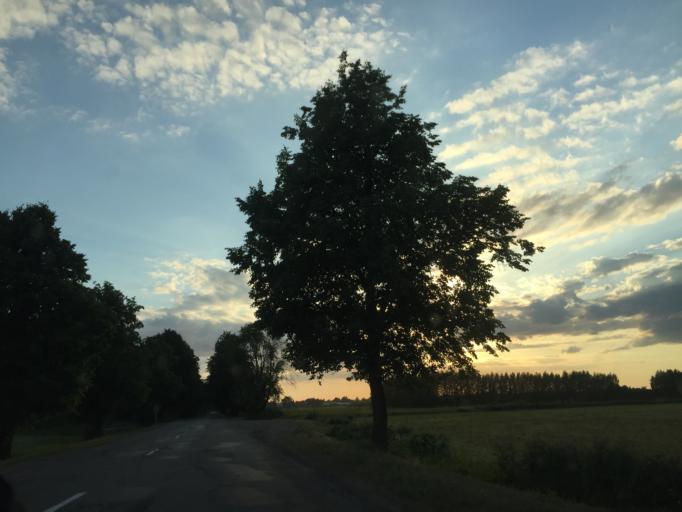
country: LV
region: Sigulda
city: Sigulda
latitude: 57.1383
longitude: 24.8855
